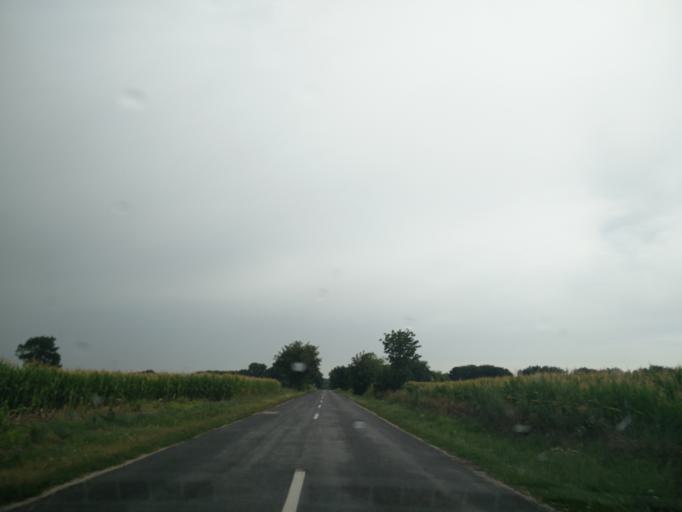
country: HU
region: Fejer
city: Bicske
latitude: 47.4332
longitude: 18.6527
